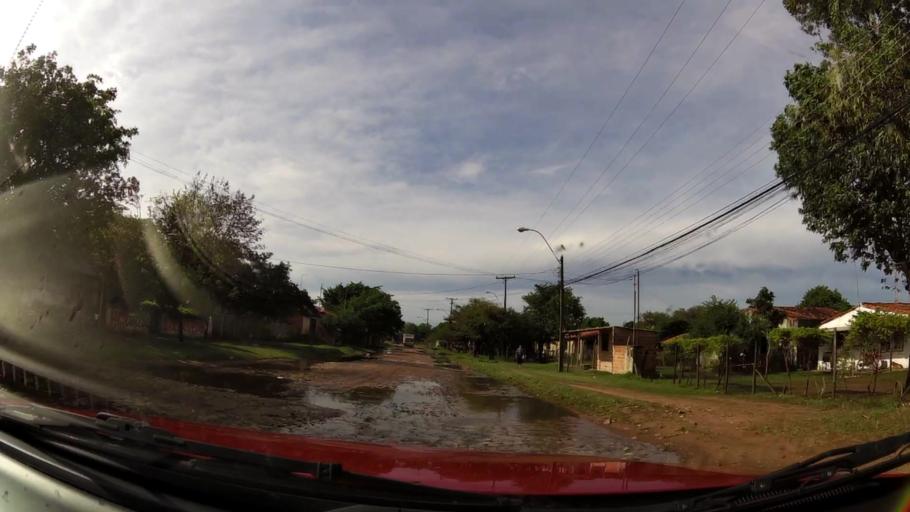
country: PY
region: Central
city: Limpio
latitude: -25.1698
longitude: -57.4892
